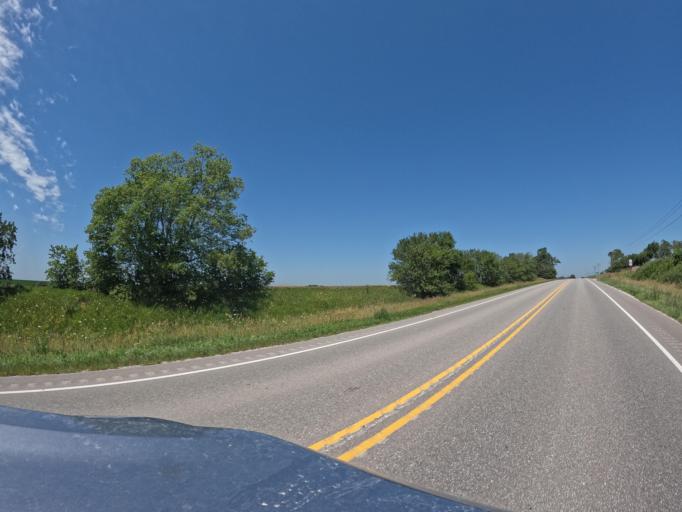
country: US
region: Iowa
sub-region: Keokuk County
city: Sigourney
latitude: 41.4498
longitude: -92.3551
